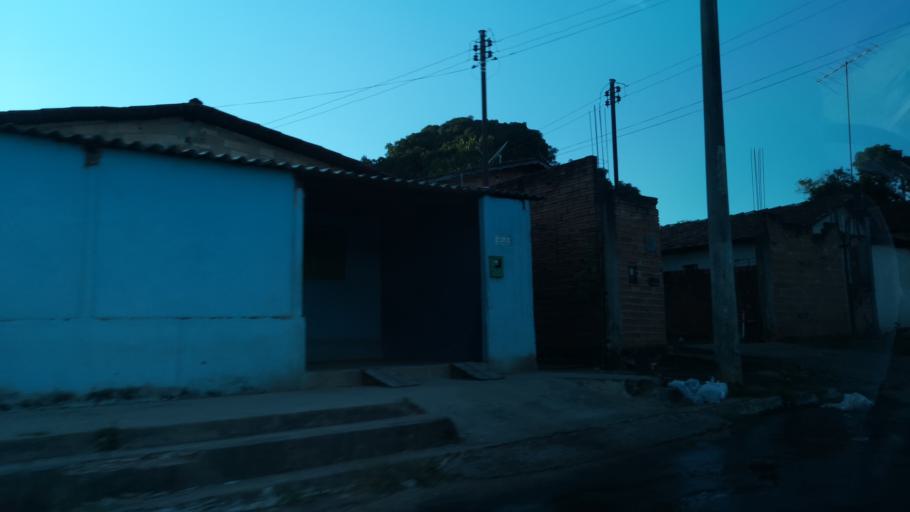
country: BR
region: Goias
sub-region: Goiania
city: Goiania
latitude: -16.6912
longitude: -49.1879
